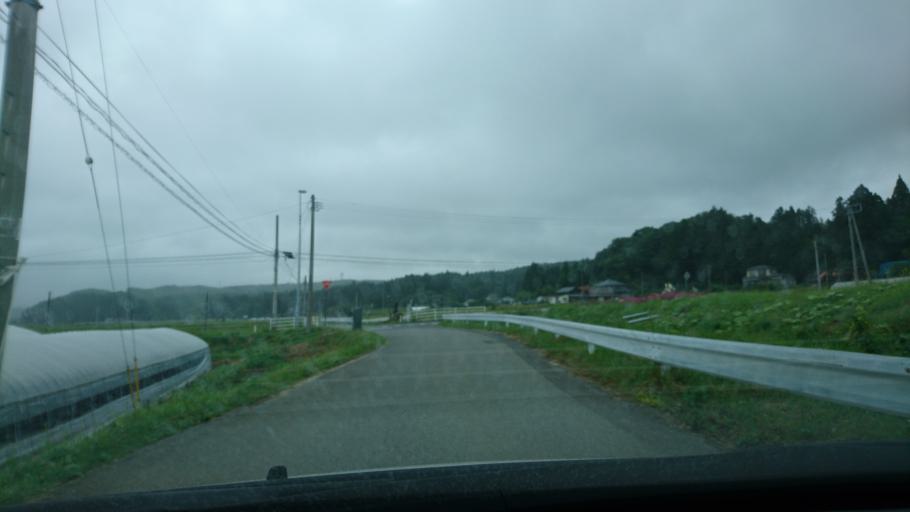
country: JP
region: Iwate
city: Ichinoseki
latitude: 38.9496
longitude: 141.0519
